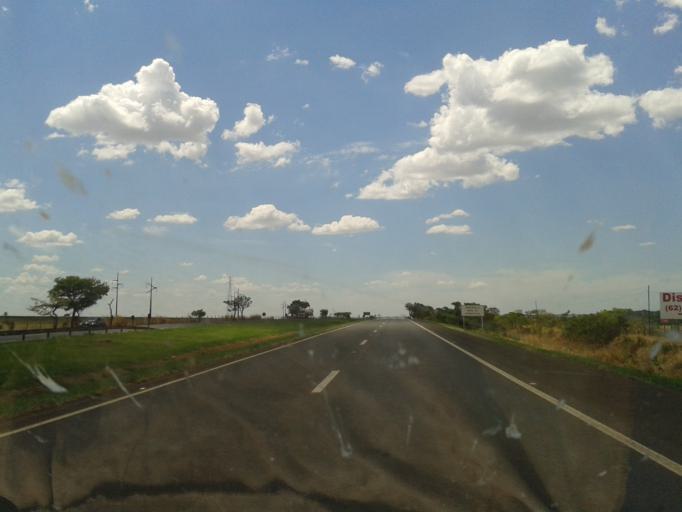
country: BR
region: Minas Gerais
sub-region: Uberlandia
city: Uberlandia
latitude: -19.0525
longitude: -48.1956
